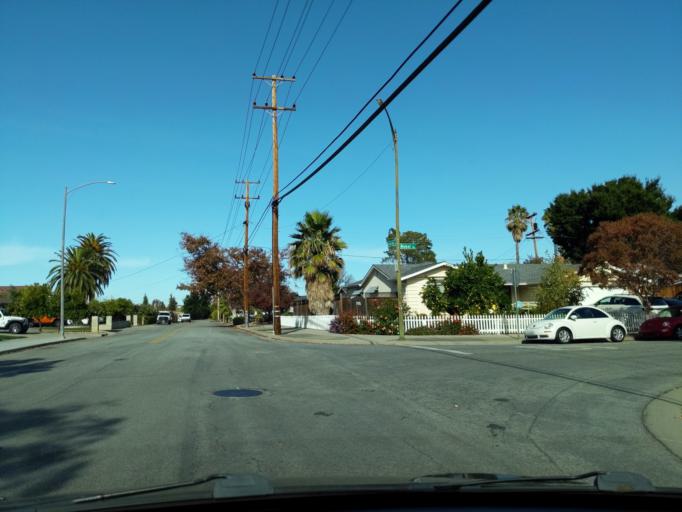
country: US
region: California
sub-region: Santa Clara County
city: Cambrian Park
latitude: 37.2486
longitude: -121.9070
